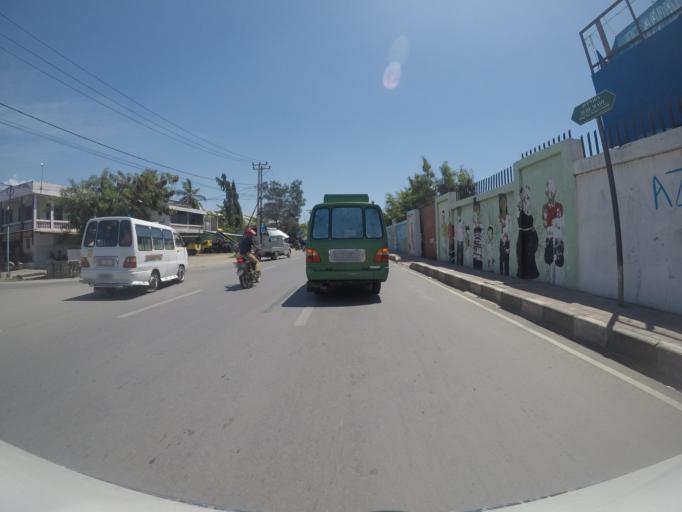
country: TL
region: Dili
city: Dili
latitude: -8.5560
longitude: 125.5829
